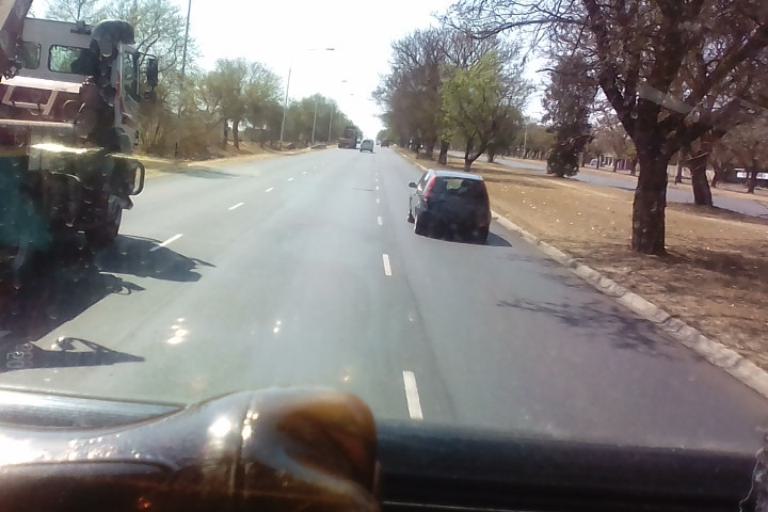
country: ZA
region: Gauteng
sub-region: Ekurhuleni Metropolitan Municipality
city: Boksburg
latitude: -26.2370
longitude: 28.2471
